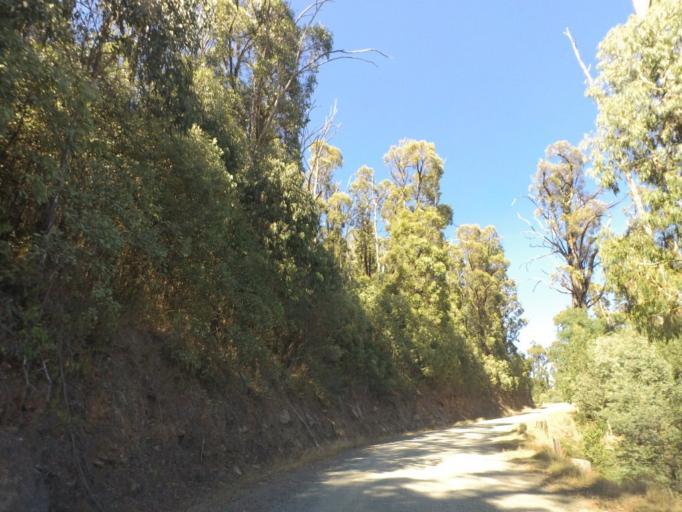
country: AU
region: Victoria
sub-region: Yarra Ranges
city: Millgrove
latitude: -37.5382
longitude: 145.7484
